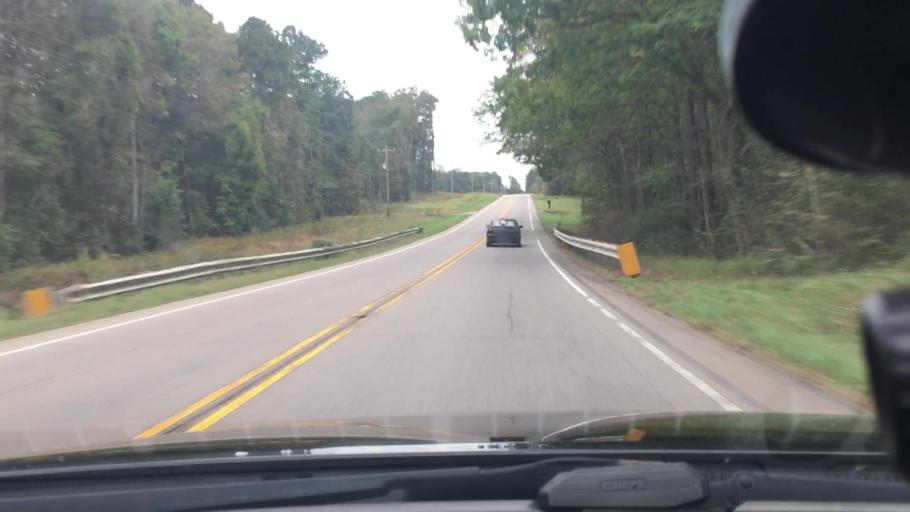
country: US
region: North Carolina
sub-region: Moore County
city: Robbins
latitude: 35.3976
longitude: -79.5367
